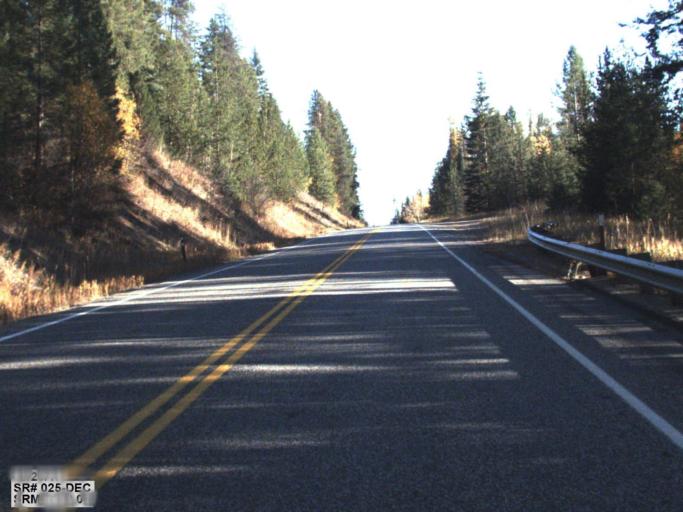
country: CA
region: British Columbia
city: Rossland
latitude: 48.9728
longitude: -117.8157
